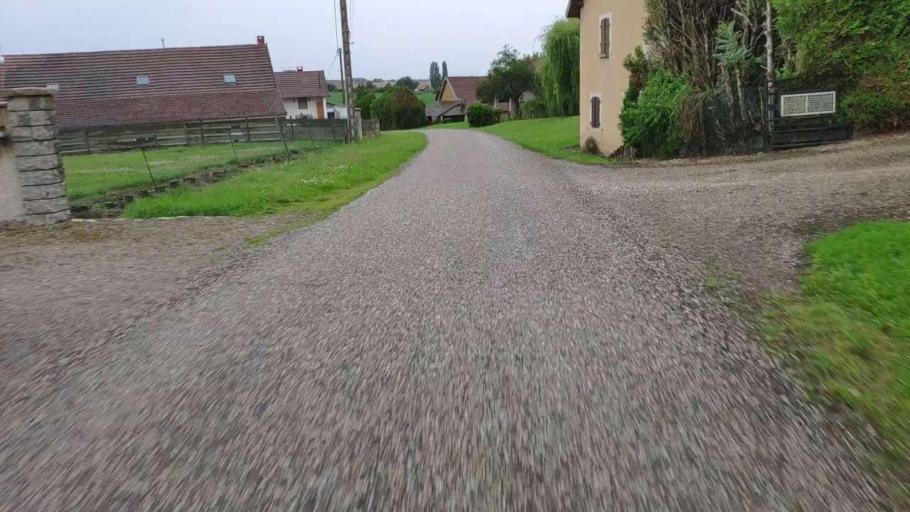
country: FR
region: Franche-Comte
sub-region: Departement du Jura
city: Chaussin
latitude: 46.8755
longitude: 5.4150
